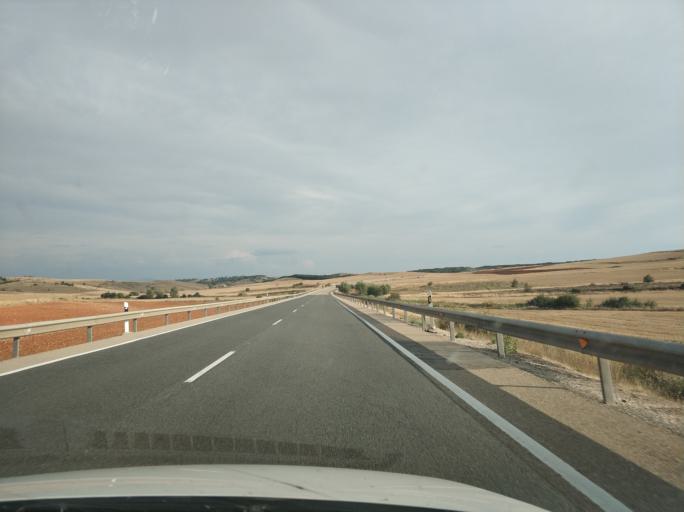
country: ES
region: Castille and Leon
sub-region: Provincia de Burgos
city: Huermeces
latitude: 42.5340
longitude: -3.7303
